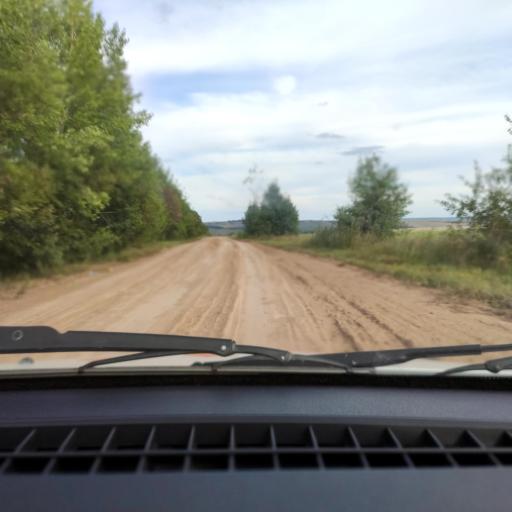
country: RU
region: Bashkortostan
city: Blagoveshchensk
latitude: 55.0988
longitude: 55.8108
